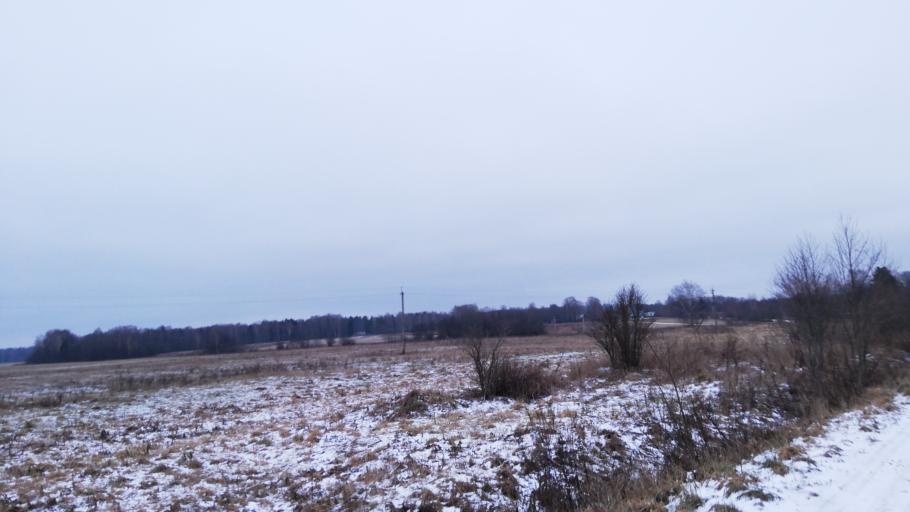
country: RU
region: Kostroma
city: Krasnoye-na-Volge
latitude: 57.6726
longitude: 41.1947
